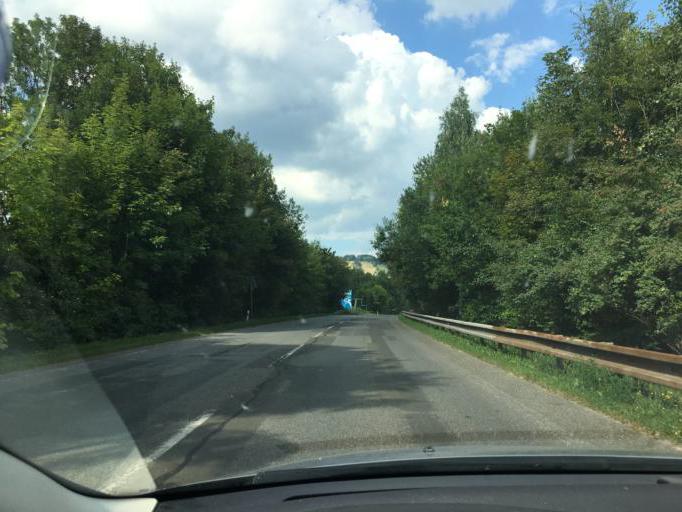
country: CZ
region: Kralovehradecky
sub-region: Okres Trutnov
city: Vrchlabi
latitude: 50.6314
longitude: 15.6004
